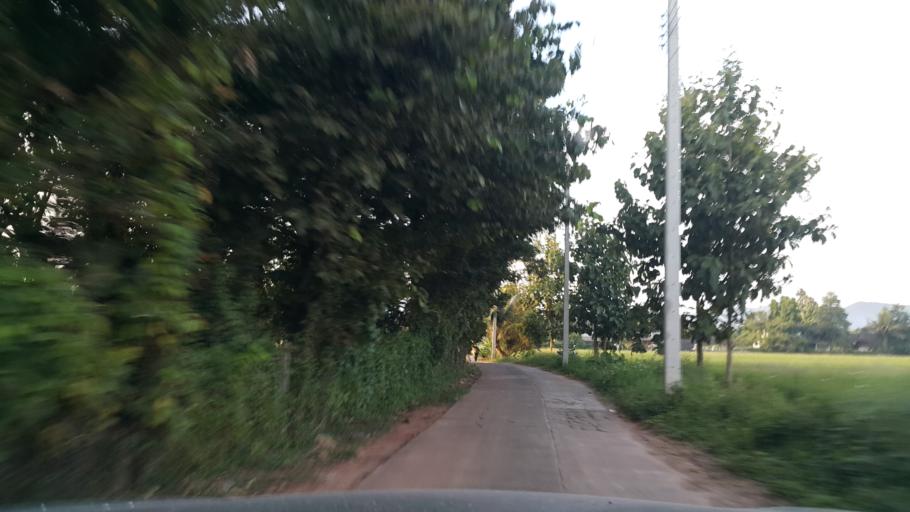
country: TH
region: Chiang Mai
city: San Sai
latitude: 18.8885
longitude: 99.0850
